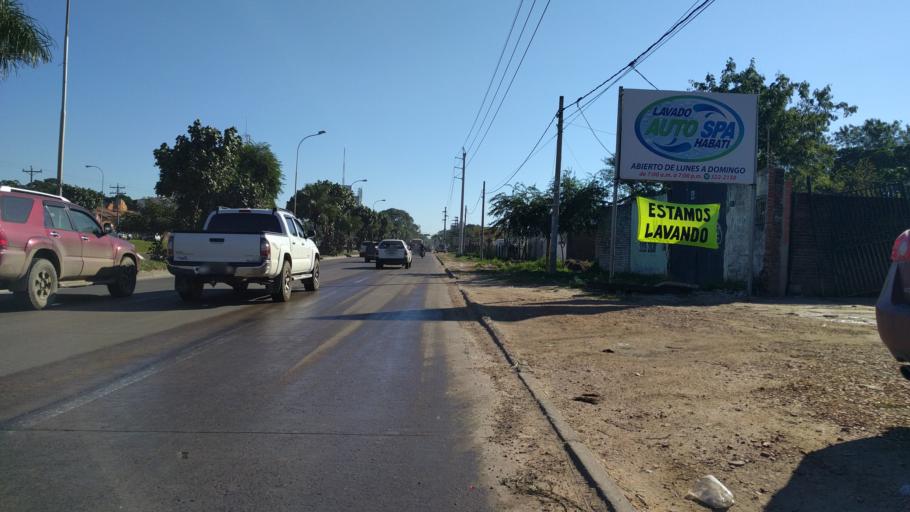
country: BO
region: Santa Cruz
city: Santa Cruz de la Sierra
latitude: -17.7892
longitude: -63.2165
